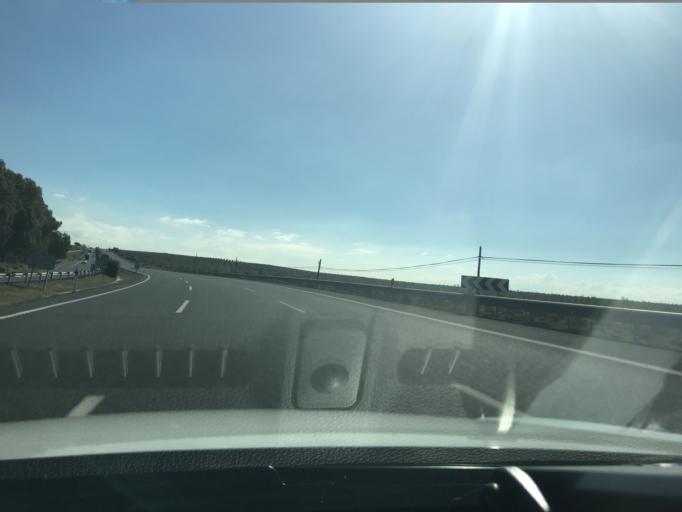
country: ES
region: Andalusia
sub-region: Provincia de Sevilla
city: La Luisiana
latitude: 37.5262
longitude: -5.2860
